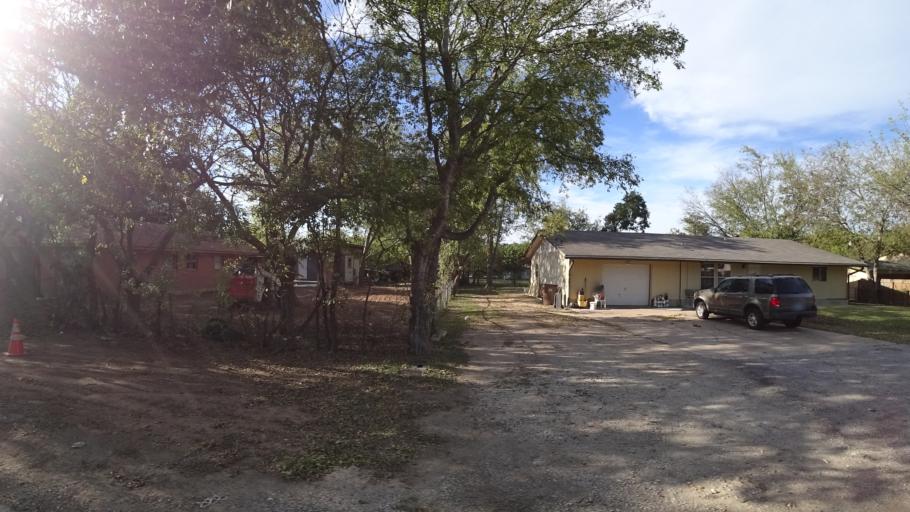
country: US
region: Texas
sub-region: Travis County
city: Wells Branch
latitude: 30.4741
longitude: -97.6857
